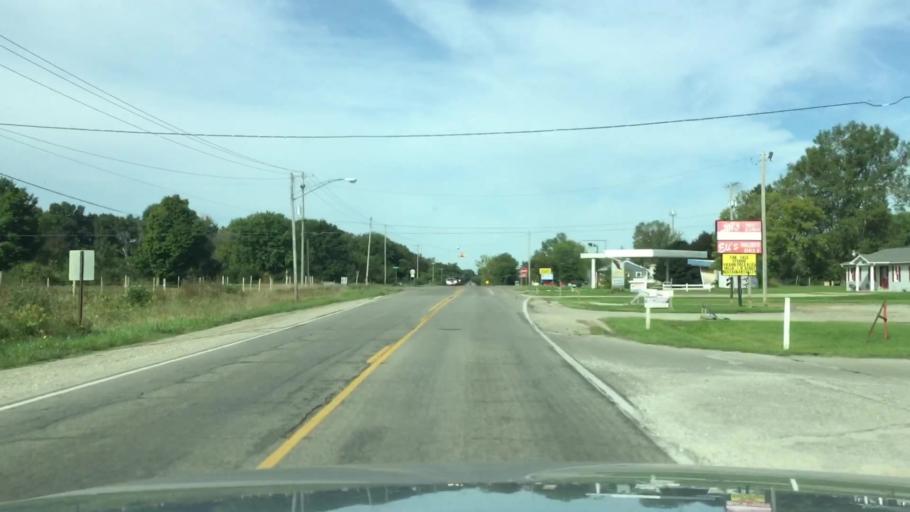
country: US
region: Michigan
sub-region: Genesee County
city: Flushing
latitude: 43.1177
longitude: -83.8513
